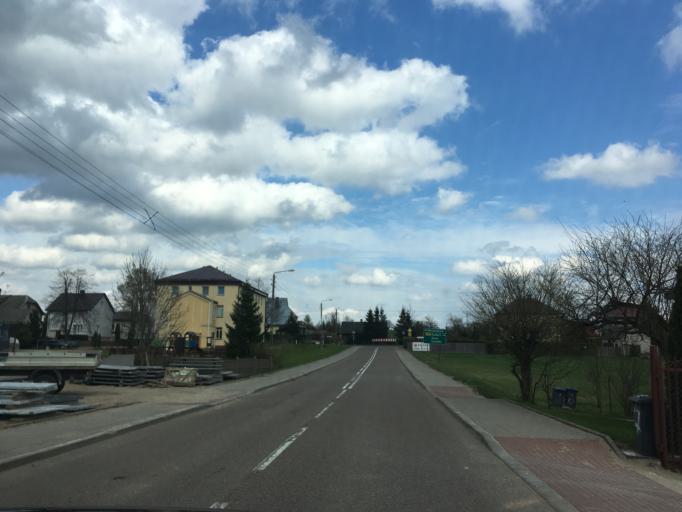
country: PL
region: Podlasie
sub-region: Suwalki
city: Suwalki
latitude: 54.3634
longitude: 22.8662
